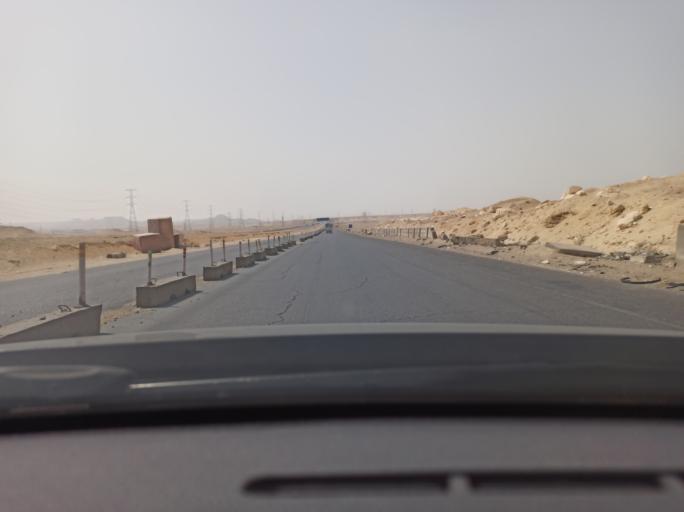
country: EG
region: Muhafazat Bani Suwayf
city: Bush
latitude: 29.1716
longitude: 31.2420
